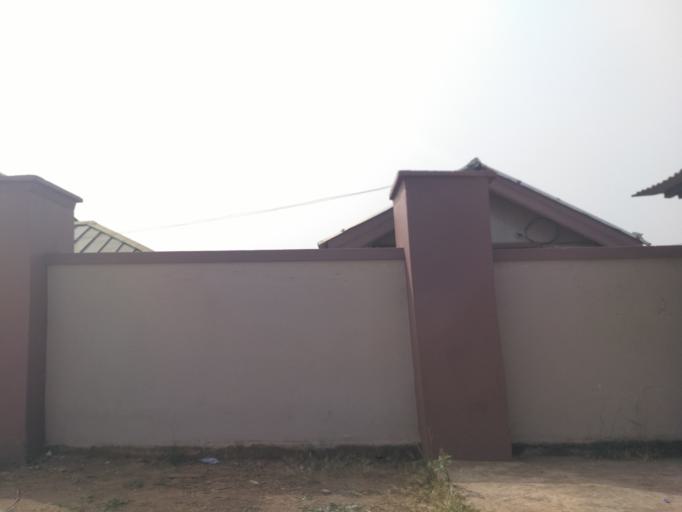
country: GH
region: Ashanti
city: Kumasi
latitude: 6.6786
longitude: -1.6053
